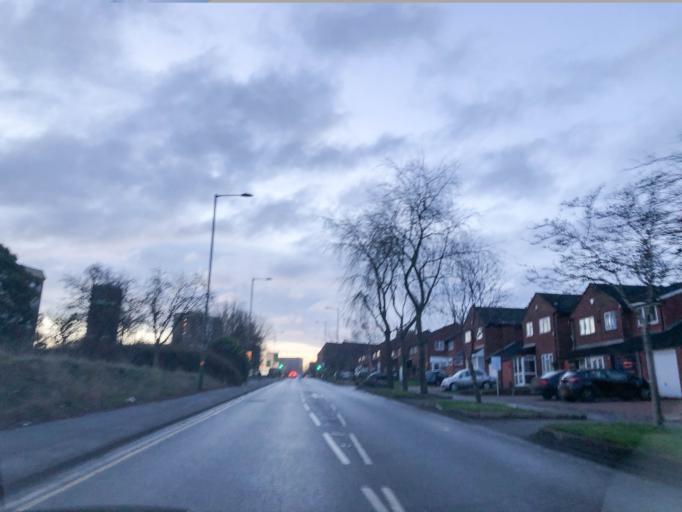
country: GB
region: England
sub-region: City and Borough of Birmingham
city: Hockley
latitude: 52.4795
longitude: -1.9295
